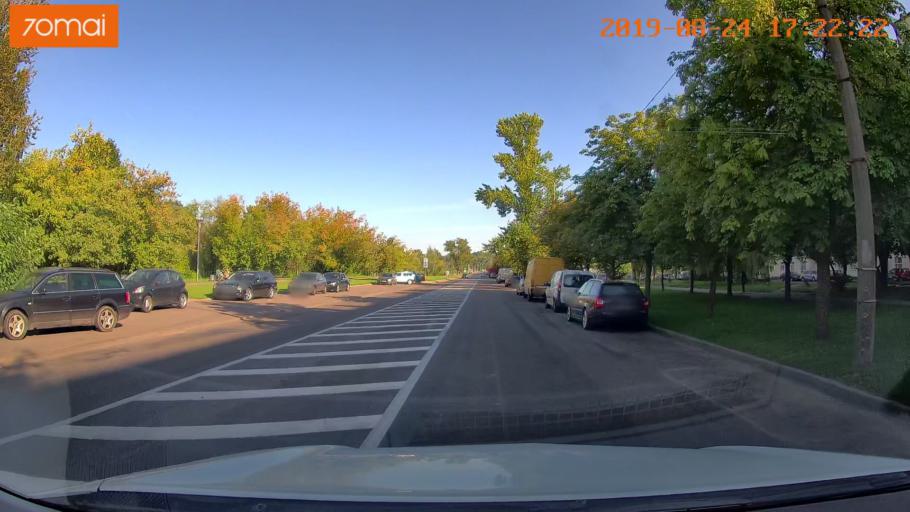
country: BY
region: Minsk
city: Hatava
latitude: 53.8462
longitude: 27.6435
